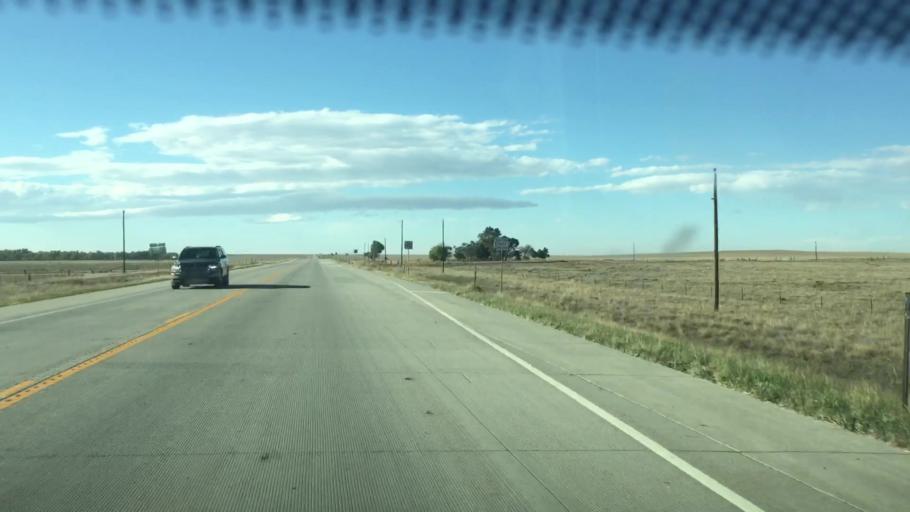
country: US
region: Colorado
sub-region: Lincoln County
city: Hugo
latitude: 39.0493
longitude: -103.3477
